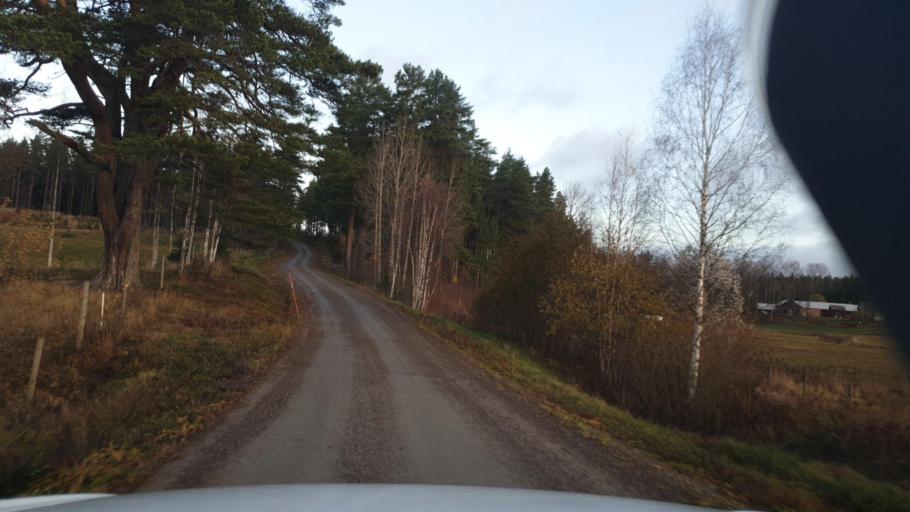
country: SE
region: Vaermland
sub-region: Arvika Kommun
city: Arvika
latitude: 59.5664
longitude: 12.7411
